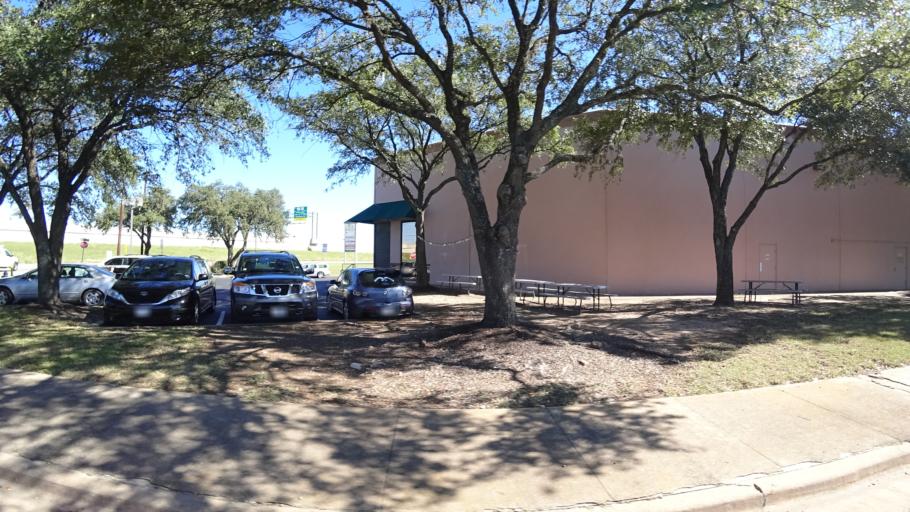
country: US
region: Texas
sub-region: Travis County
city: Rollingwood
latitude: 30.2309
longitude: -97.8036
